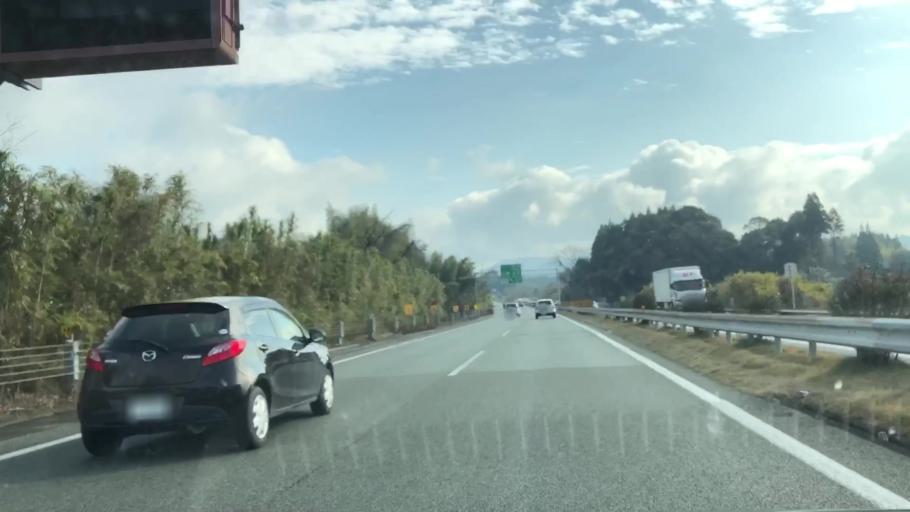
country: JP
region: Kumamoto
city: Tamana
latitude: 32.9908
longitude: 130.6028
